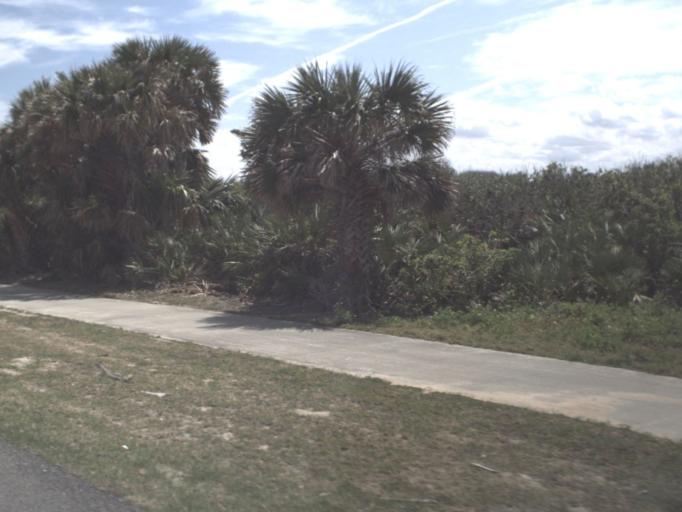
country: US
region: Florida
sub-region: Flagler County
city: Flagler Beach
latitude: 29.5369
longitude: -81.1556
